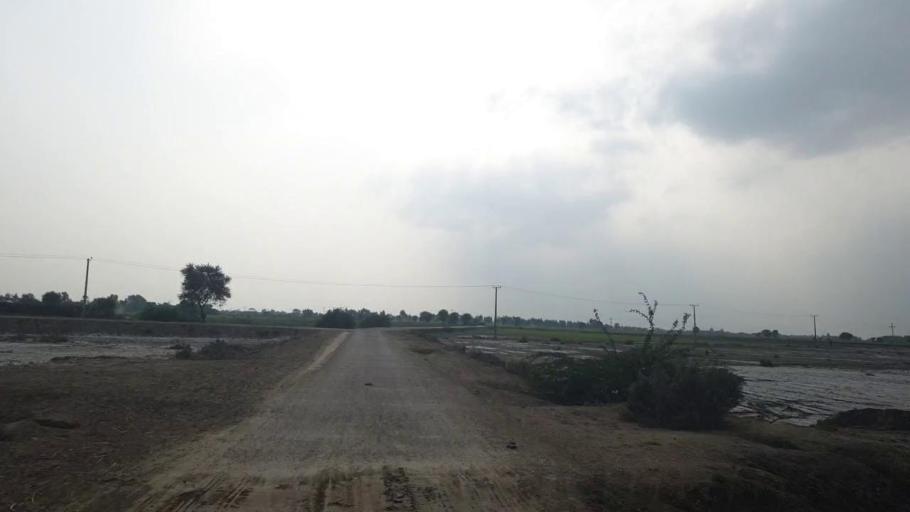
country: PK
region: Sindh
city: Badin
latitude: 24.6441
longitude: 68.6966
